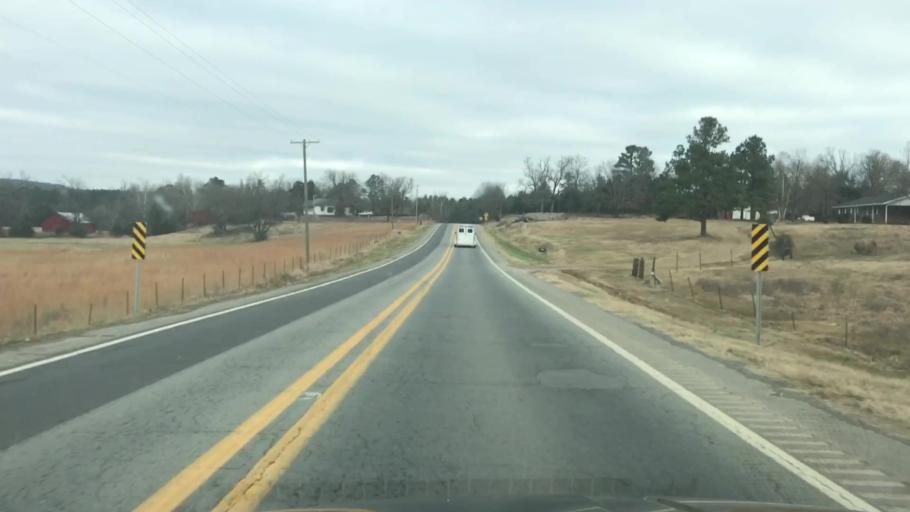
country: US
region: Arkansas
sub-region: Scott County
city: Waldron
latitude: 34.9479
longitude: -94.1046
